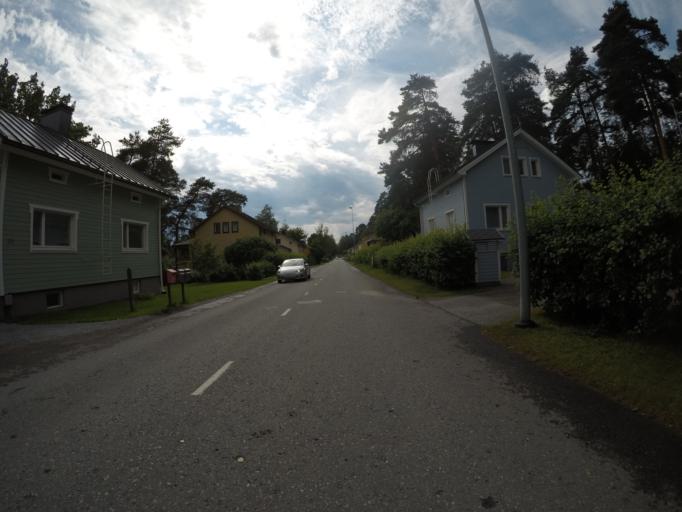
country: FI
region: Haeme
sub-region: Haemeenlinna
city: Haemeenlinna
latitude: 61.0125
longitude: 24.4702
